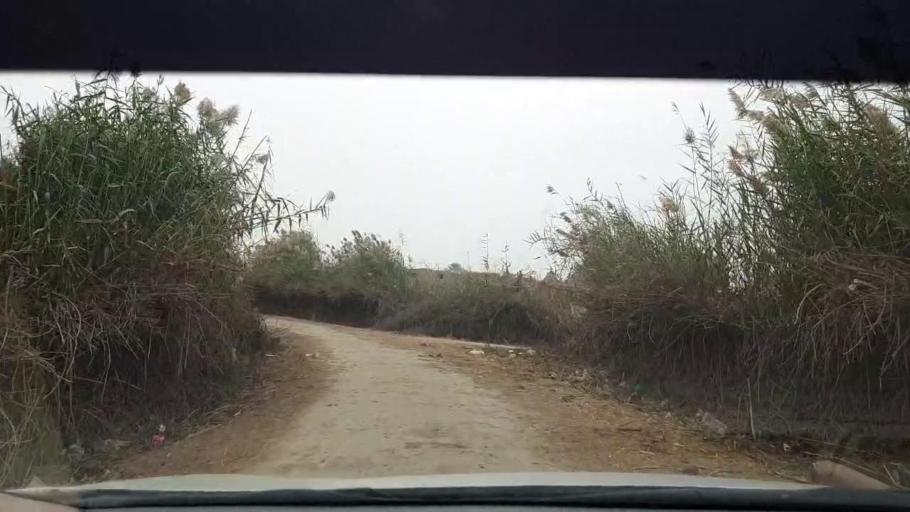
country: PK
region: Sindh
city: Berani
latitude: 25.8560
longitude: 68.7926
